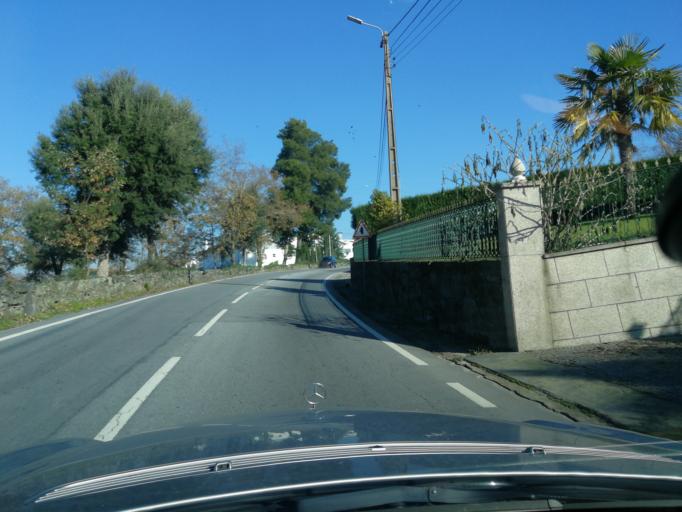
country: PT
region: Braga
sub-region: Braga
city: Adaufe
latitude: 41.6099
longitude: -8.4253
